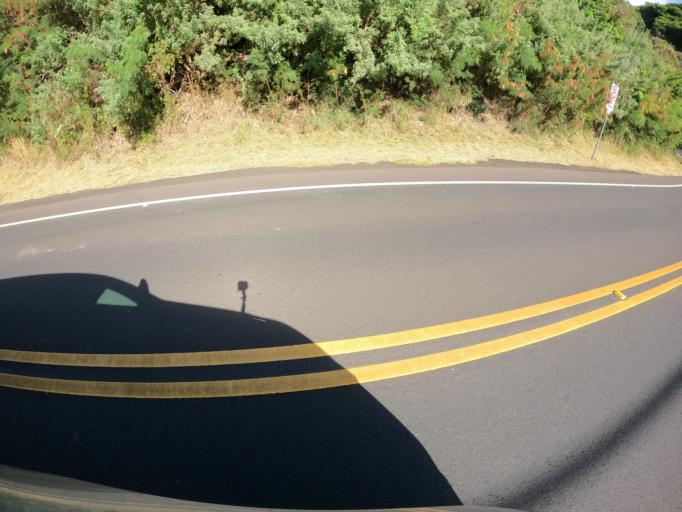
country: US
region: Hawaii
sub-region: Honolulu County
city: Halawa Heights
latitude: 21.3812
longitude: -157.9143
